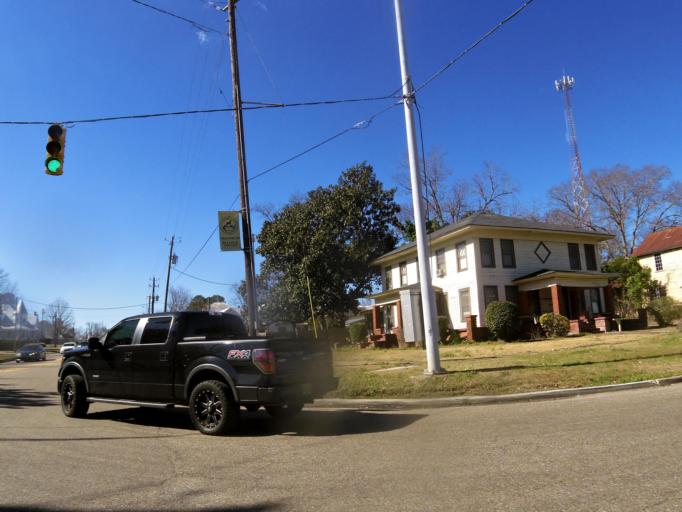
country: US
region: Alabama
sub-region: Bullock County
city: Union Springs
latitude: 32.1435
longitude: -85.7135
